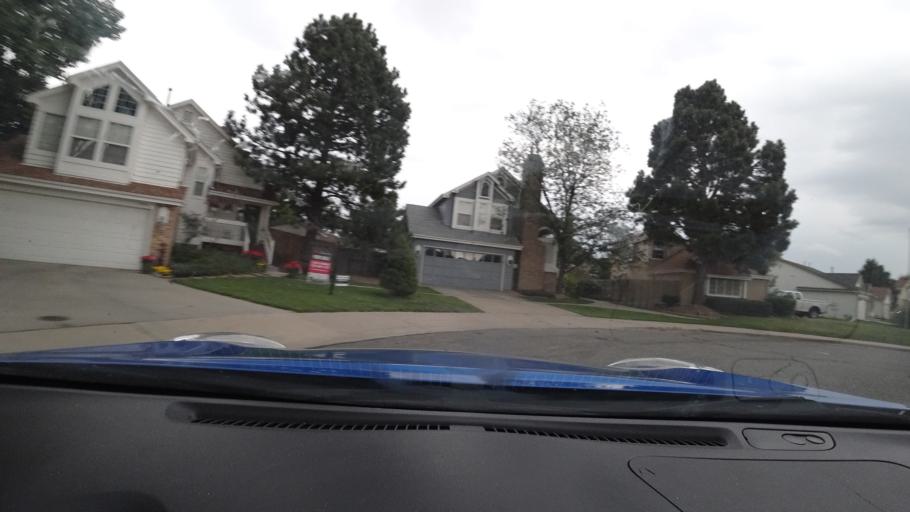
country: US
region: Colorado
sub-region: Adams County
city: Aurora
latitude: 39.7775
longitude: -104.7590
